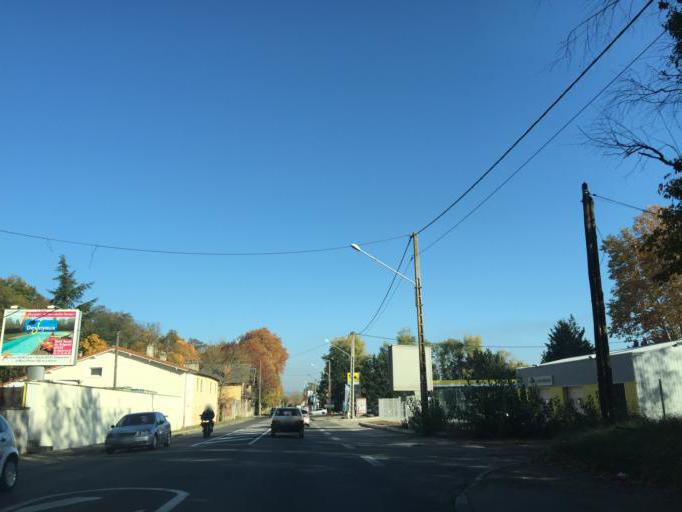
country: FR
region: Rhone-Alpes
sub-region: Departement du Rhone
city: Brignais
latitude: 45.6563
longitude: 4.7511
